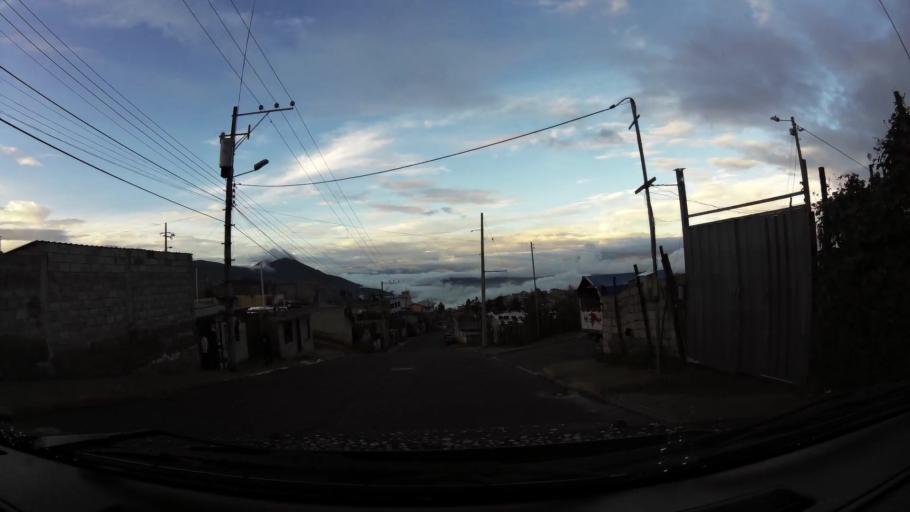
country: EC
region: Pichincha
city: Quito
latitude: -0.1028
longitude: -78.5245
